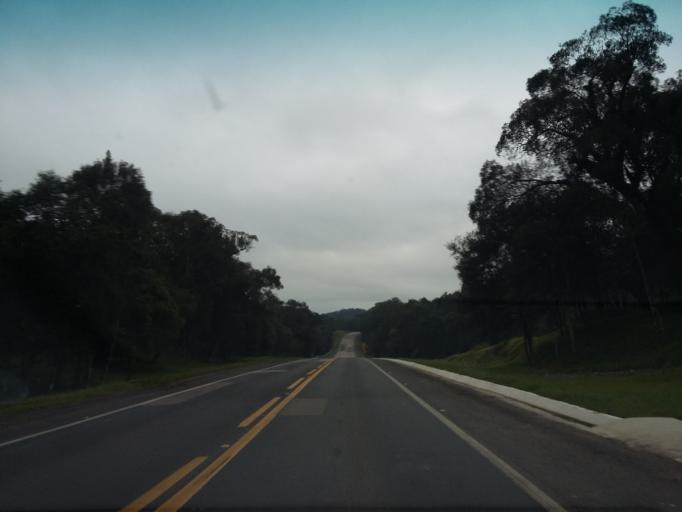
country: BR
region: Santa Catarina
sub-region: Santa Cecilia
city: Santa Cecilia
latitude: -26.6958
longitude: -50.2937
